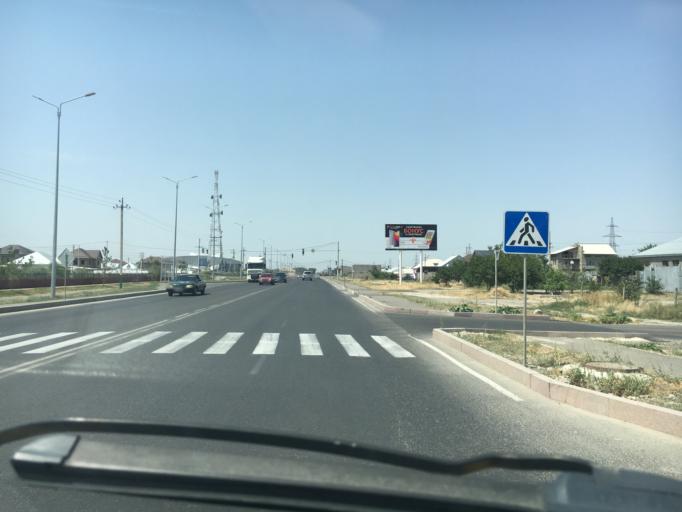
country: KZ
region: Zhambyl
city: Taraz
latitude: 42.8821
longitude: 71.3215
